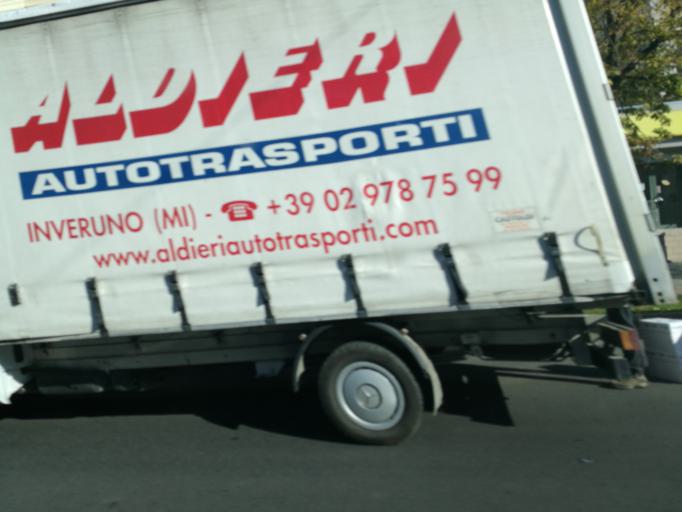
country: RO
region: Iasi
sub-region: Municipiul Iasi
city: Iasi
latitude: 47.1737
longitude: 27.5583
